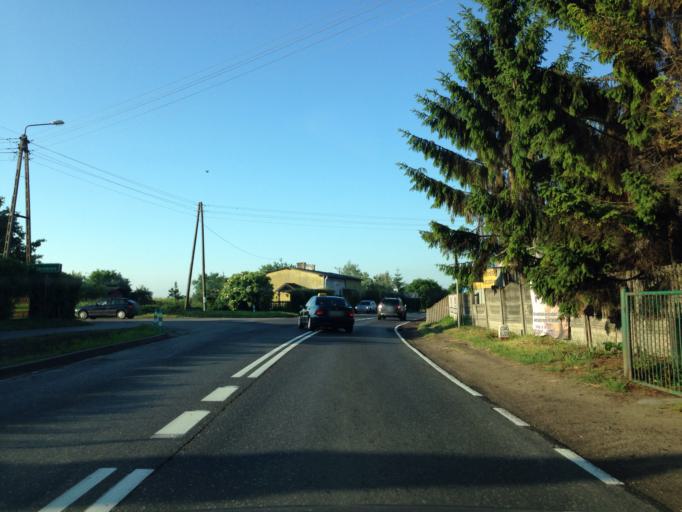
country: PL
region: Pomeranian Voivodeship
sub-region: Powiat kwidzynski
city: Kwidzyn
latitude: 53.6910
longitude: 18.9681
